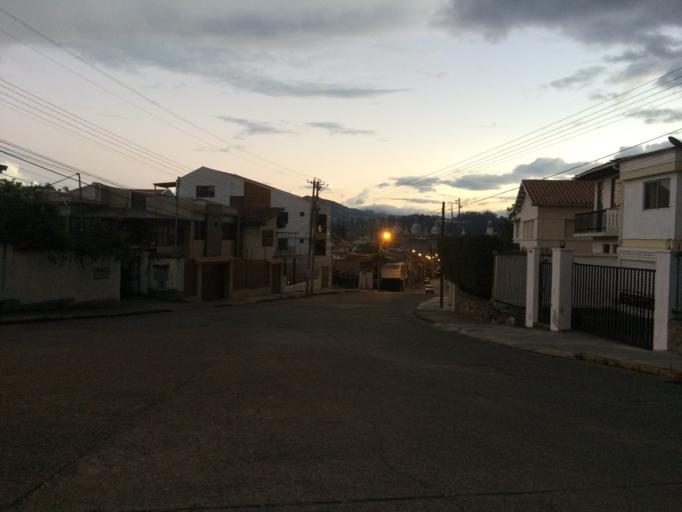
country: EC
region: Azuay
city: Cuenca
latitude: -2.8897
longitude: -79.0046
